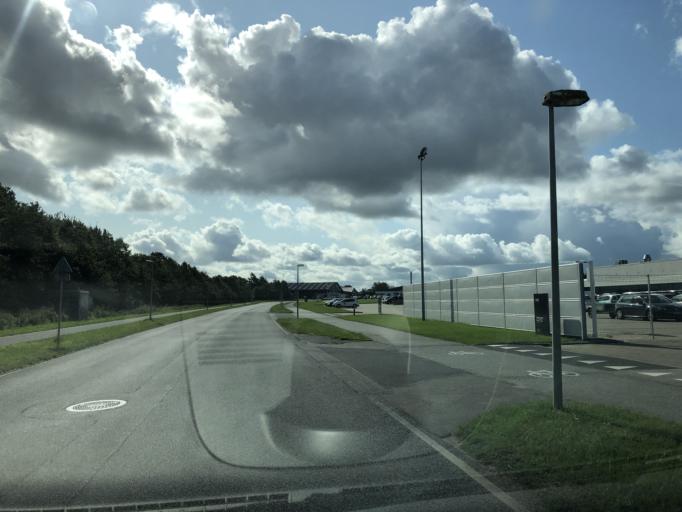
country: DK
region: Central Jutland
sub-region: Herning Kommune
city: Lind
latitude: 56.1134
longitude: 8.9785
